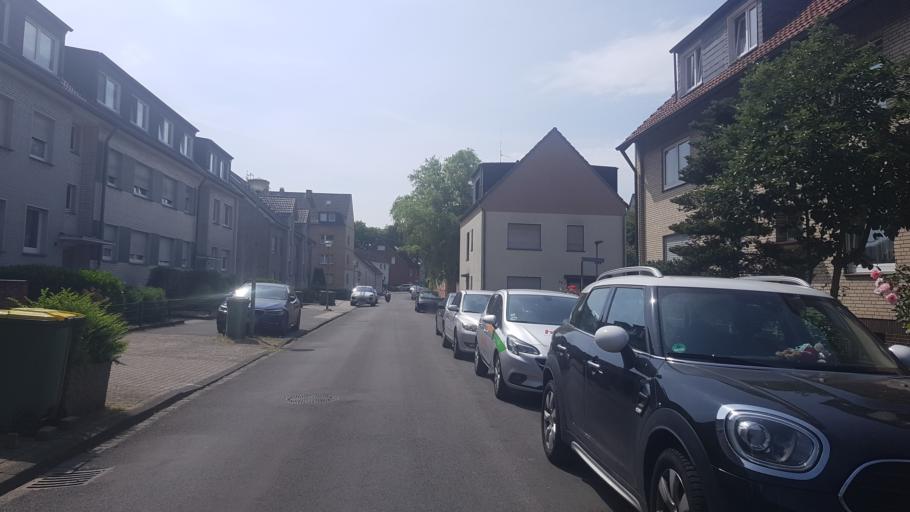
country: DE
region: North Rhine-Westphalia
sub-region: Regierungsbezirk Dusseldorf
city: Oberhausen
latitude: 51.4732
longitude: 6.8912
